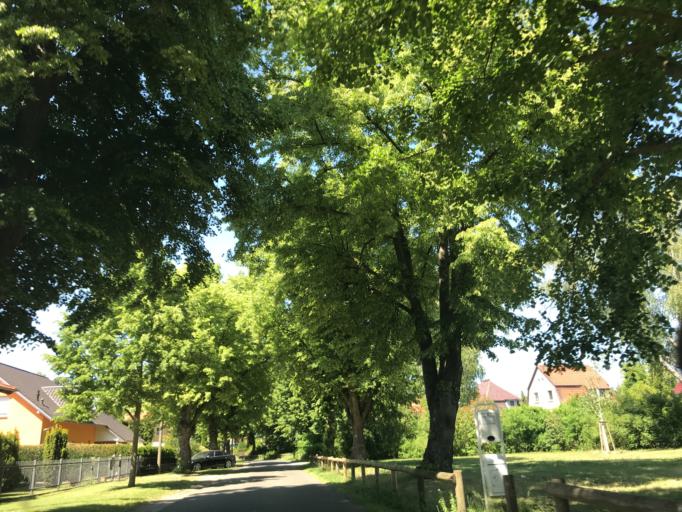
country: DE
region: Berlin
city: Falkenhagener Feld
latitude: 52.5681
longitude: 13.1428
